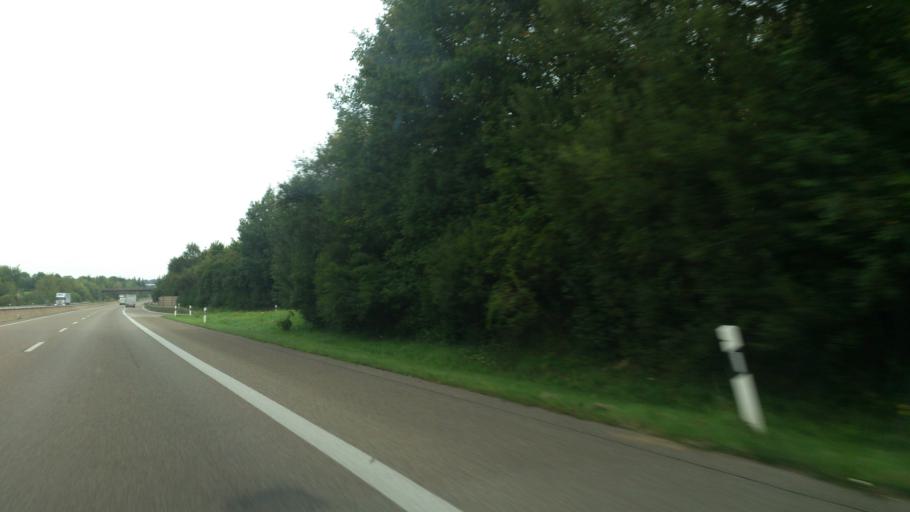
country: DE
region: North Rhine-Westphalia
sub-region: Regierungsbezirk Koln
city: Nettersheim
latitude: 50.4900
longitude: 6.6736
